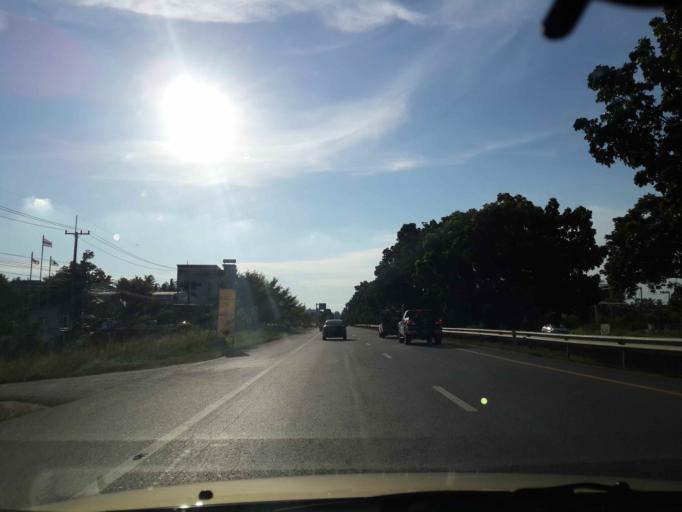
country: TH
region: Chon Buri
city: Bang Lamung
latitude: 12.9755
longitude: 100.9648
